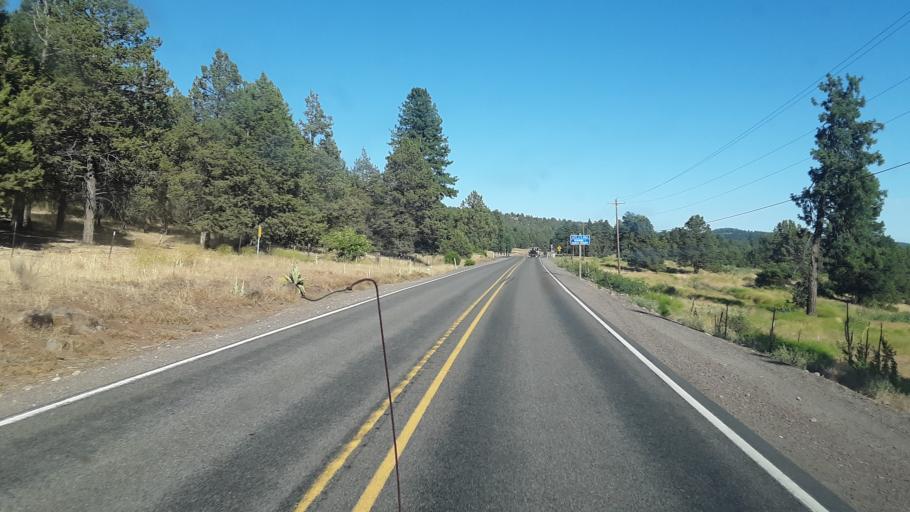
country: US
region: Oregon
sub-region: Klamath County
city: Klamath Falls
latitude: 42.2740
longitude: -121.8890
